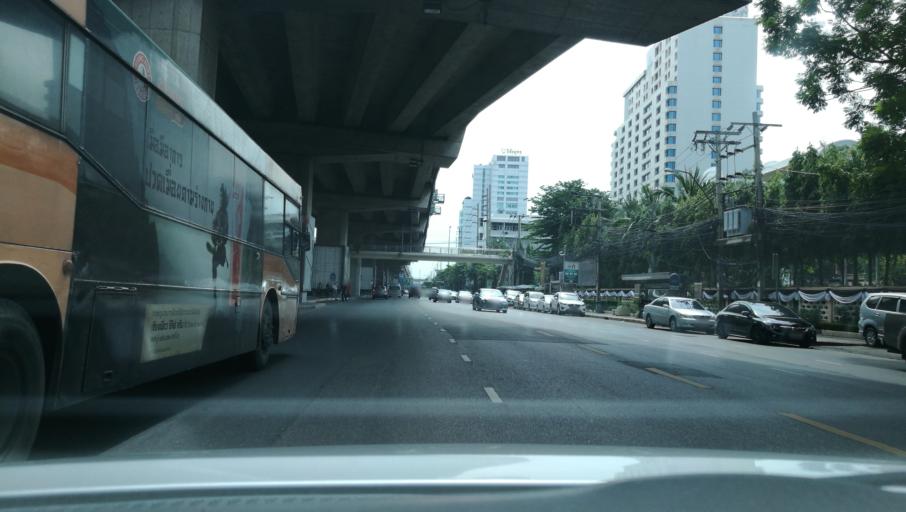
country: TH
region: Bangkok
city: Phaya Thai
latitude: 13.7847
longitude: 100.5349
